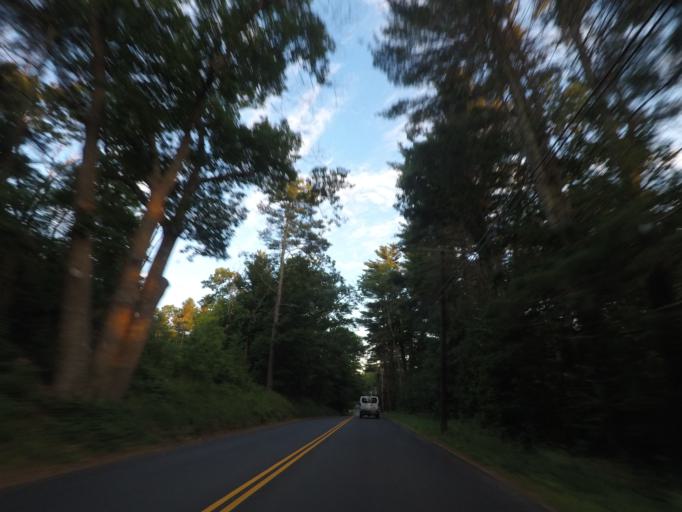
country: US
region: Massachusetts
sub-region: Worcester County
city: Fiskdale
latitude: 42.1422
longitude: -72.1296
